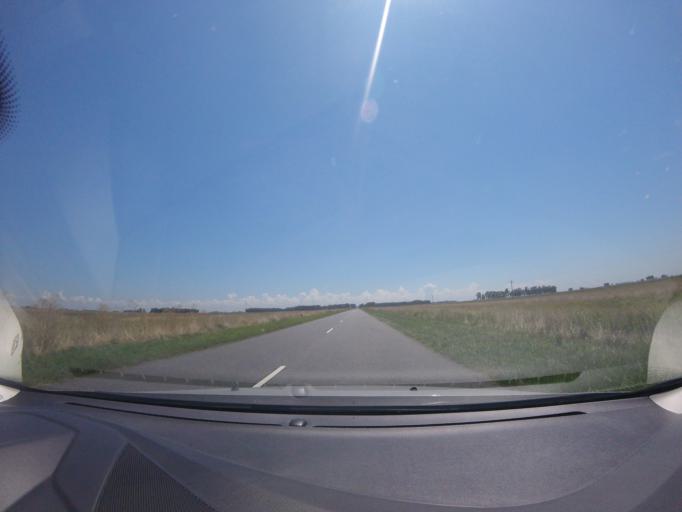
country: AR
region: Buenos Aires
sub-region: Partido de Rauch
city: Rauch
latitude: -36.4349
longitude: -59.0073
